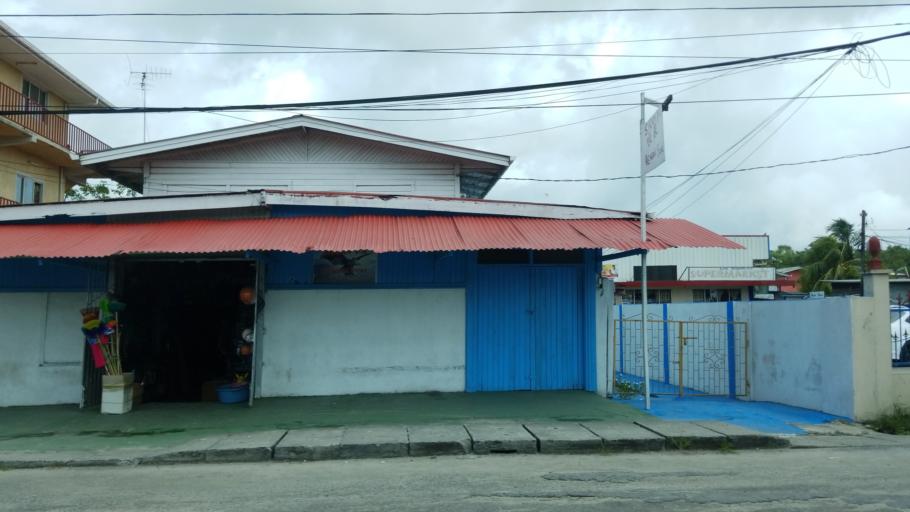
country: GY
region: Demerara-Mahaica
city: Georgetown
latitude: 6.7676
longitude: -58.1768
